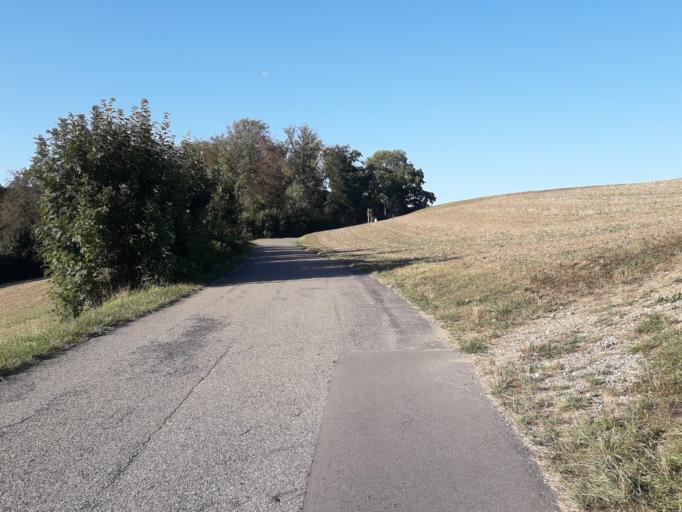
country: CH
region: Aargau
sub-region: Bezirk Baden
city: Unterehrendingen
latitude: 47.5629
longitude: 8.3599
